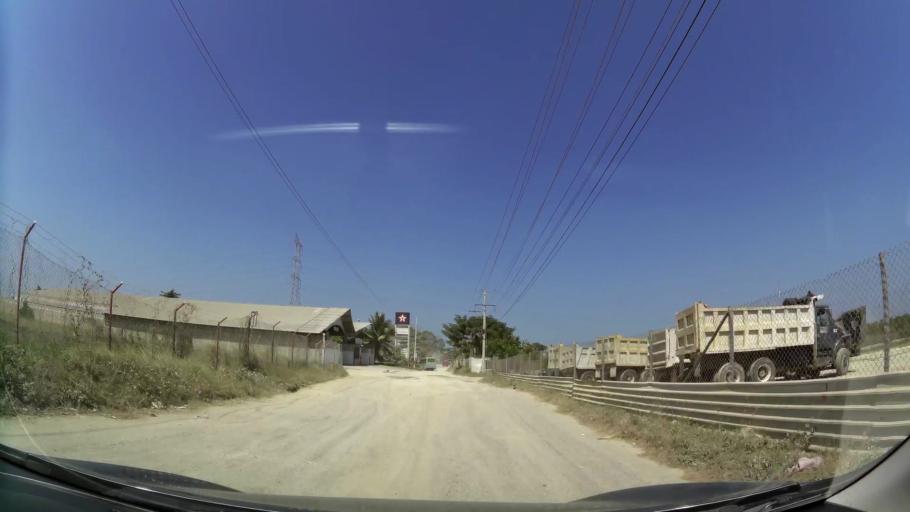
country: CO
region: Bolivar
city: Cartagena
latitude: 10.3995
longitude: -75.4558
